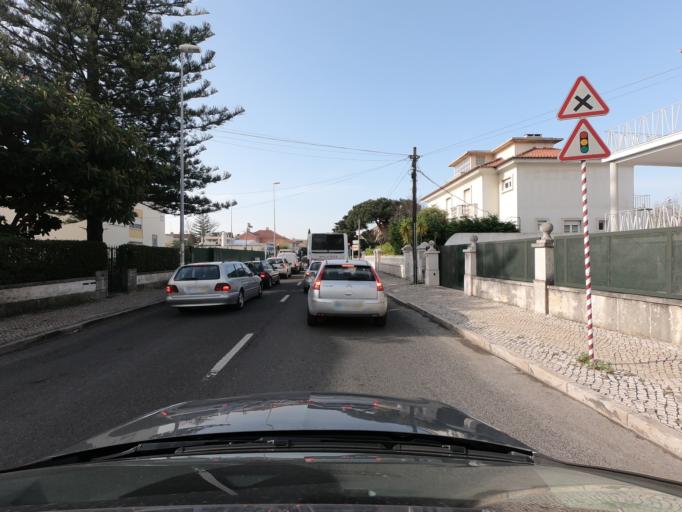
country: PT
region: Lisbon
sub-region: Oeiras
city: Carcavelos
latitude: 38.6916
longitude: -9.3184
